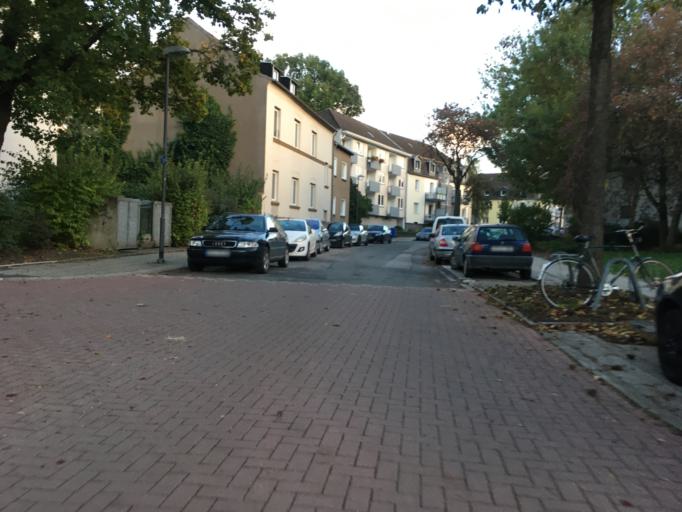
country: DE
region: North Rhine-Westphalia
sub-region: Regierungsbezirk Munster
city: Bottrop
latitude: 51.4868
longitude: 6.9250
